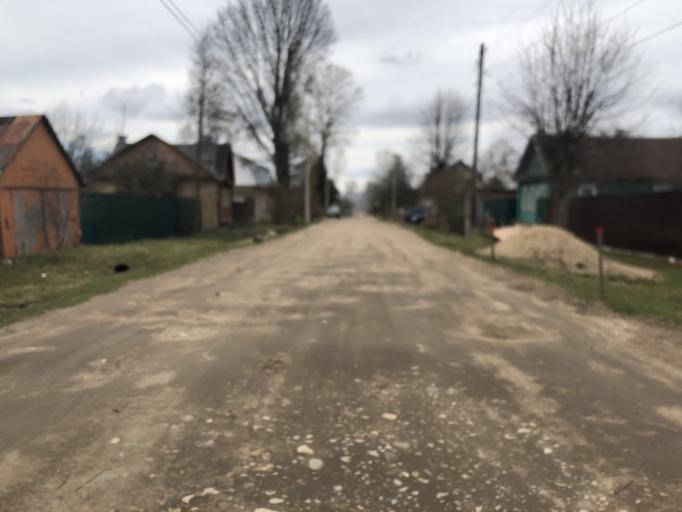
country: RU
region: Tverskaya
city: Rzhev
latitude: 56.2516
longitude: 34.3171
